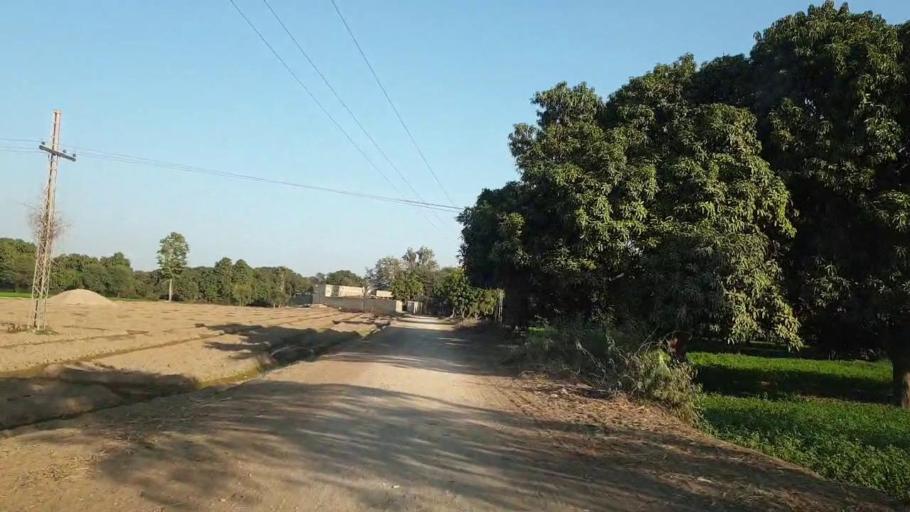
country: PK
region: Sindh
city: Tando Allahyar
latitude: 25.4971
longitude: 68.6229
